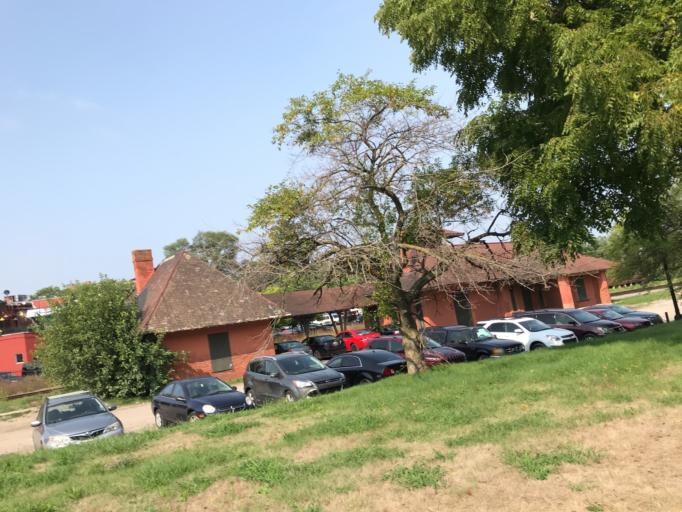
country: US
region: Michigan
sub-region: Washtenaw County
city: Ypsilanti
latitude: 42.2466
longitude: -83.6088
